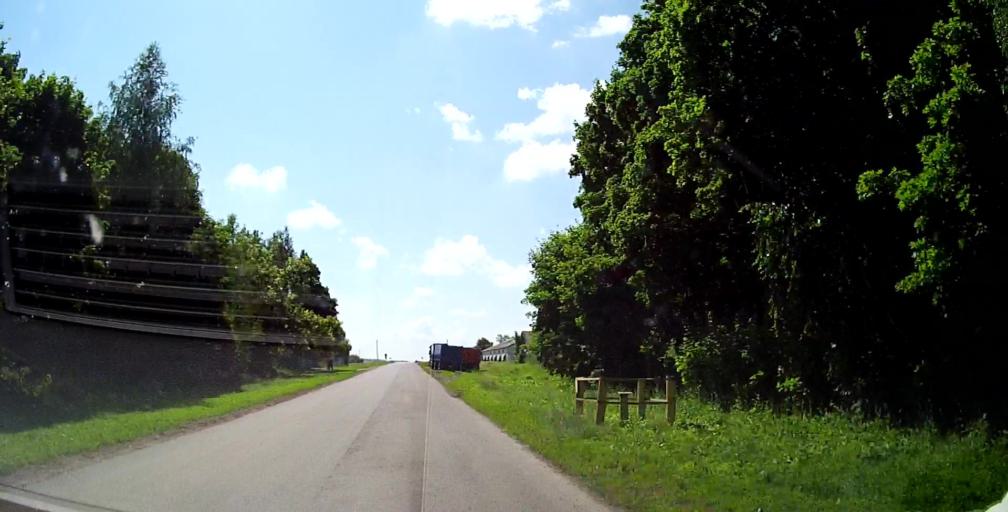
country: RU
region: Lipetsk
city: Chaplygin
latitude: 53.3194
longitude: 39.9576
